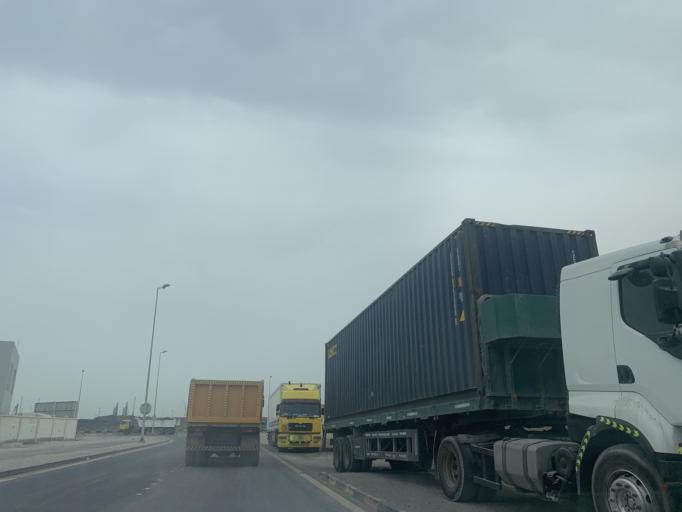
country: BH
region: Muharraq
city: Al Hadd
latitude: 26.2051
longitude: 50.6629
